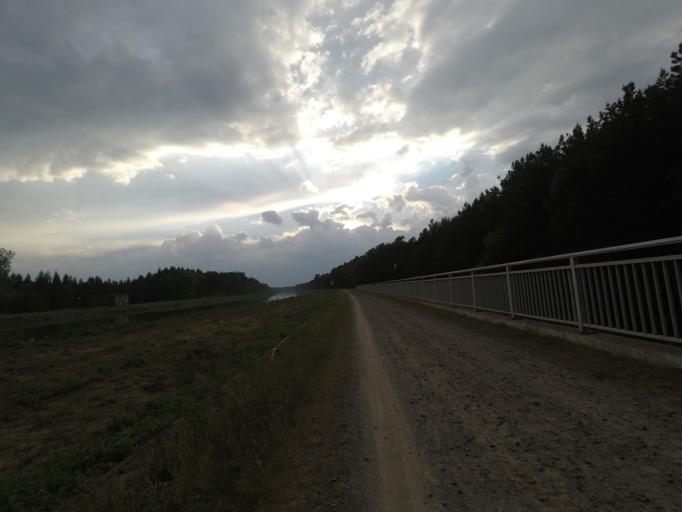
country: DE
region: Brandenburg
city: Melchow
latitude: 52.8582
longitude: 13.7293
